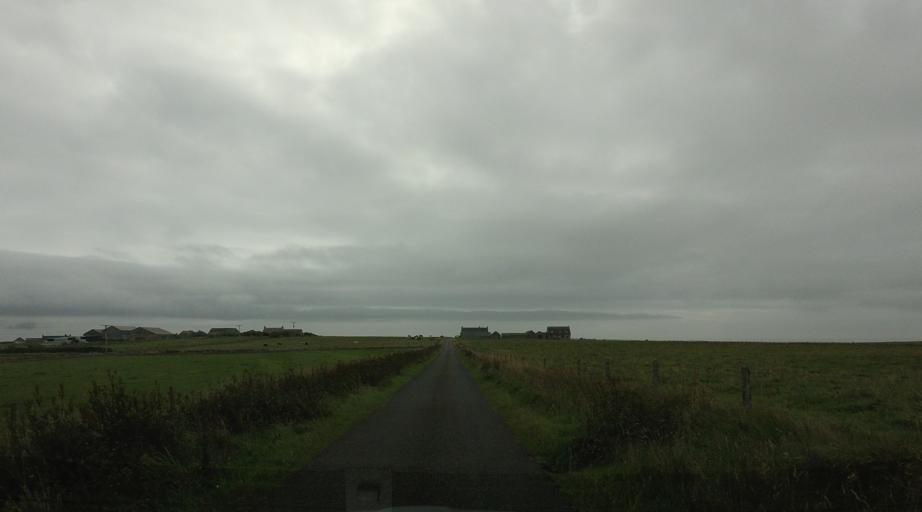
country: GB
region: Scotland
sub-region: Orkney Islands
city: Orkney
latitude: 58.7652
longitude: -2.9624
